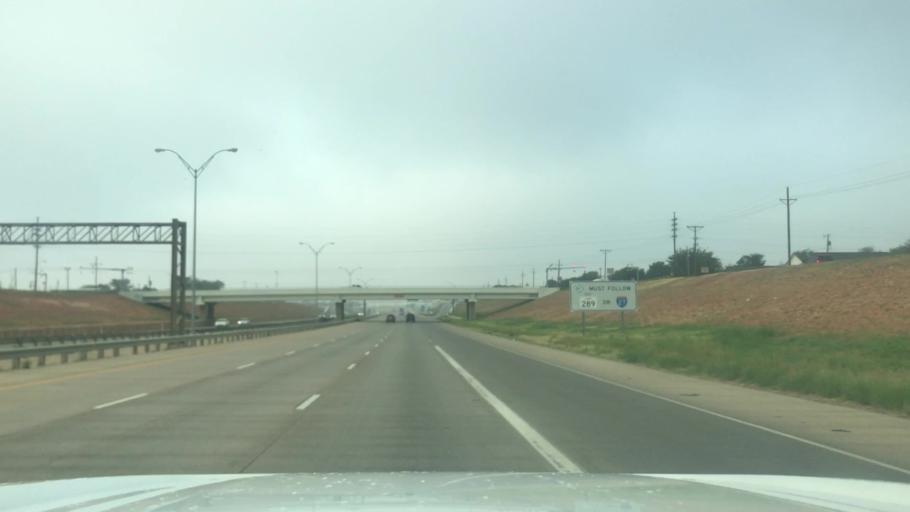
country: US
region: Texas
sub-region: Lubbock County
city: Lubbock
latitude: 33.5580
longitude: -101.8452
